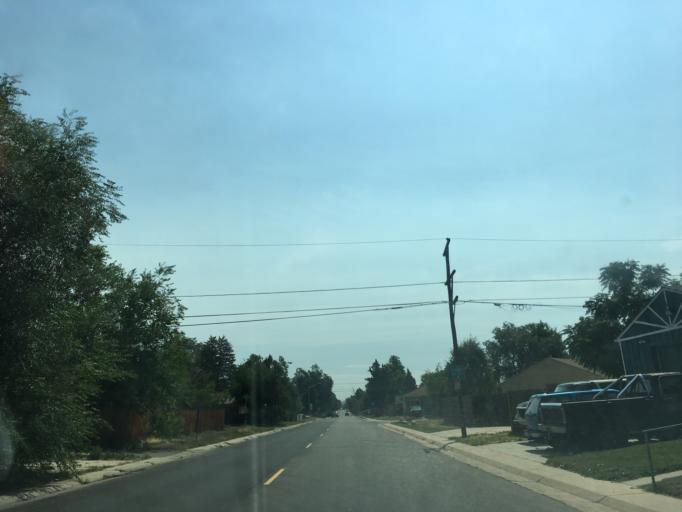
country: US
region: Colorado
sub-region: Jefferson County
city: Lakewood
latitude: 39.6932
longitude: -105.0459
